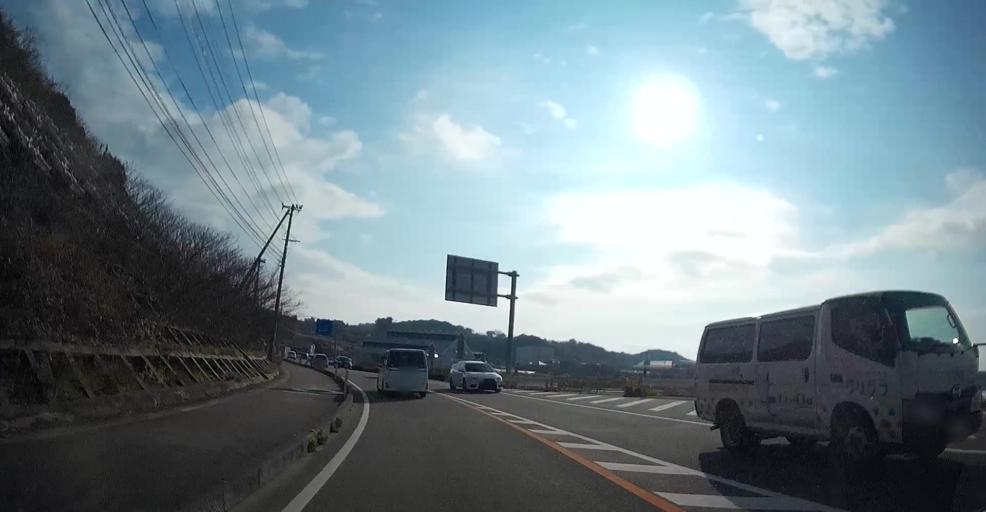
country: JP
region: Kumamoto
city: Yatsushiro
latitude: 32.5751
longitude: 130.4197
